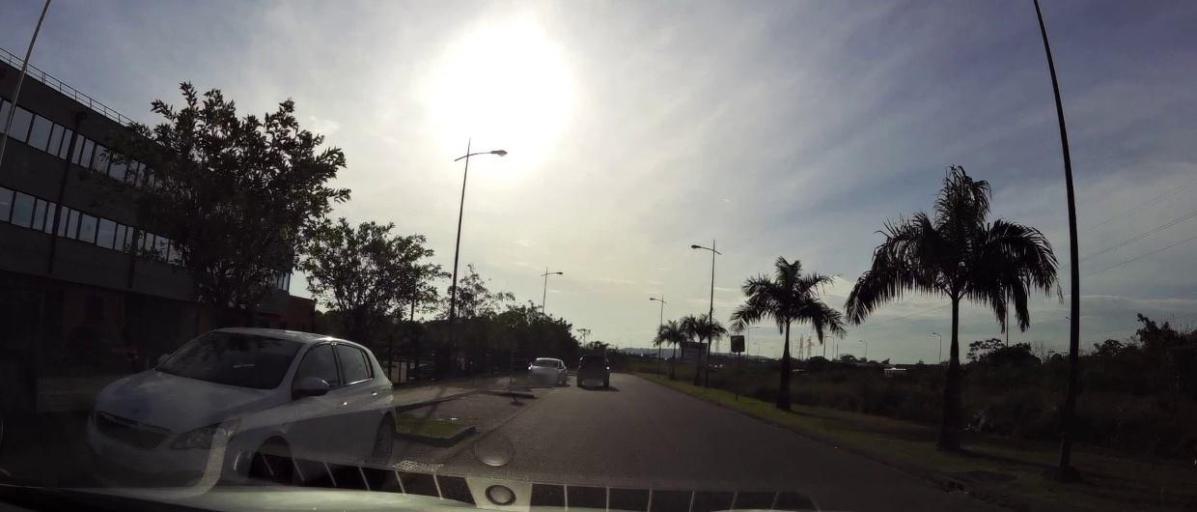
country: GF
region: Guyane
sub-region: Guyane
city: Cayenne
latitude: 4.8915
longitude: -52.3373
